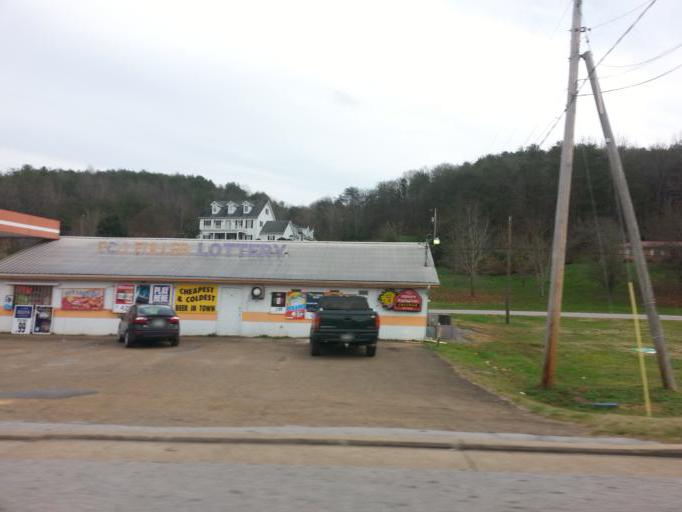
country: US
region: Tennessee
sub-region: Hamilton County
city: Sale Creek
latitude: 35.3739
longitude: -85.1134
